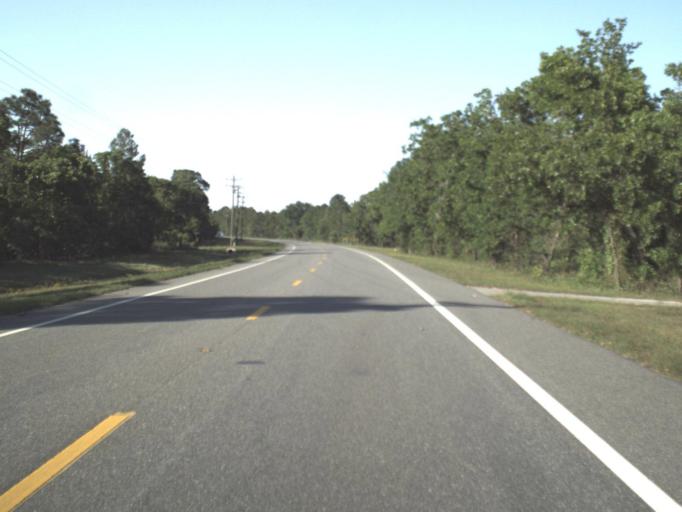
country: US
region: Florida
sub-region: Liberty County
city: Bristol
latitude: 30.4273
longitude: -84.7744
